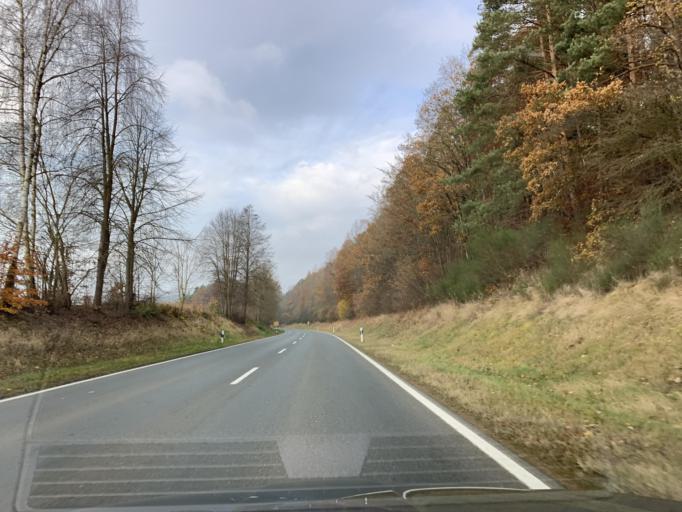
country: DE
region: Bavaria
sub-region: Upper Palatinate
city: Thanstein
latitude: 49.3488
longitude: 12.4601
